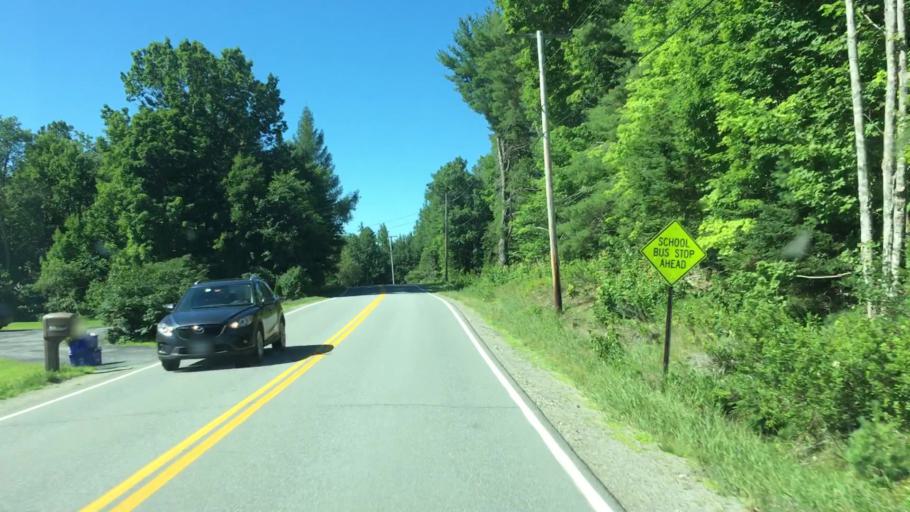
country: US
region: Maine
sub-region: Hancock County
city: Dedham
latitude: 44.7258
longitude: -68.6385
